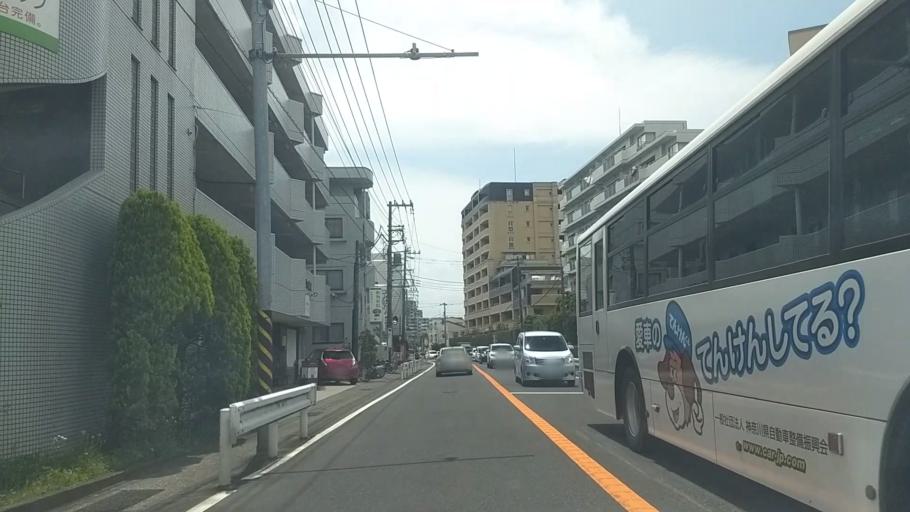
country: JP
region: Kanagawa
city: Fujisawa
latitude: 35.3484
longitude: 139.4946
